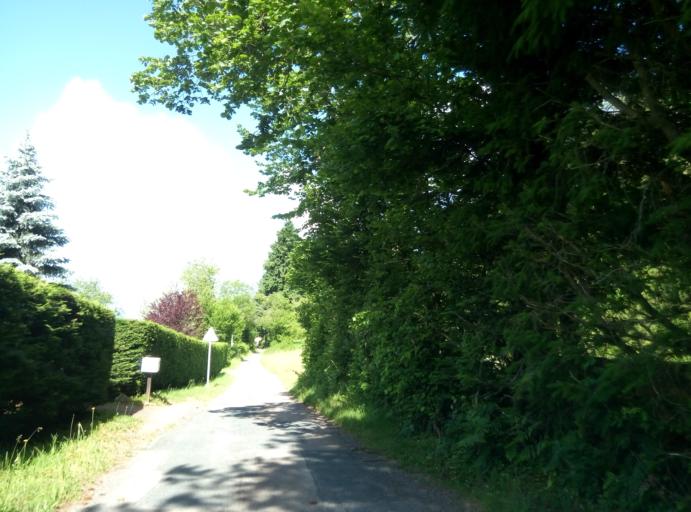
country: FR
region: Rhone-Alpes
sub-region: Departement du Rhone
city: Cublize
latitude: 45.9918
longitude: 4.4017
